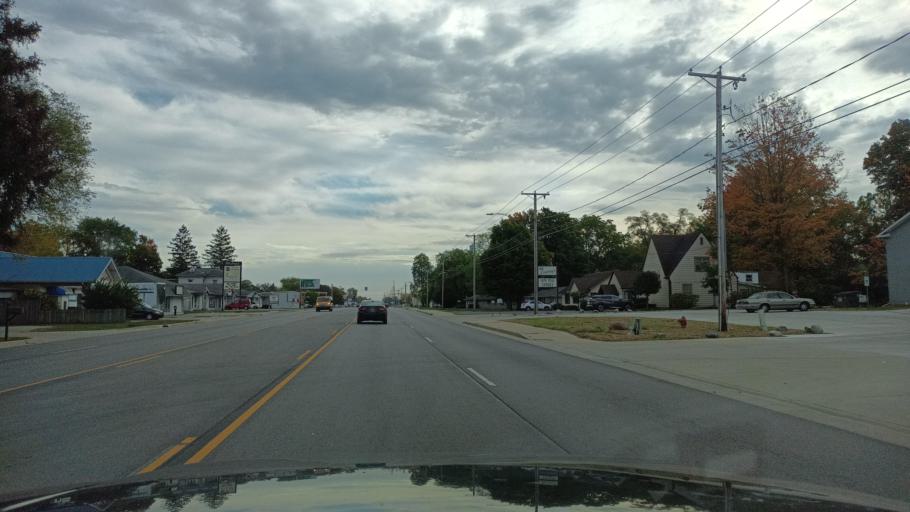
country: US
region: Indiana
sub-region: Delaware County
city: Yorktown
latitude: 40.1811
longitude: -85.4601
